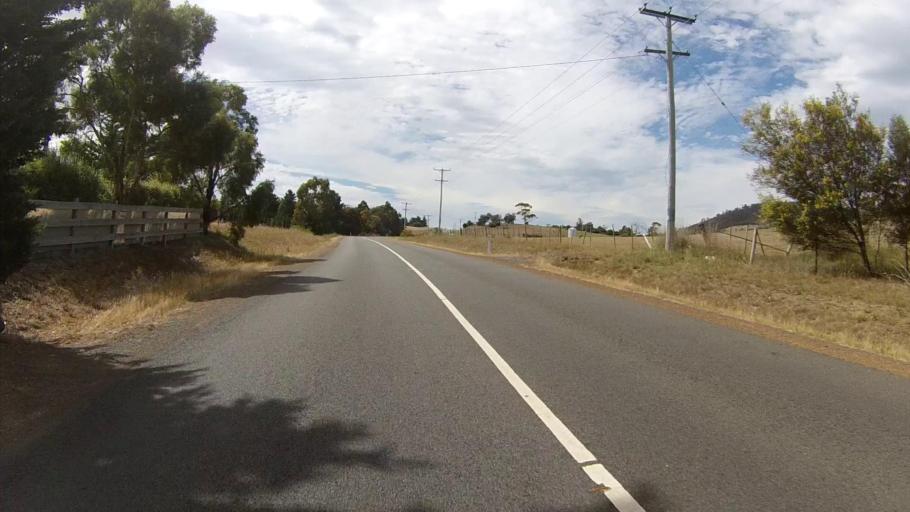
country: AU
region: Tasmania
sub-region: Brighton
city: Old Beach
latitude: -42.6956
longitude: 147.3505
